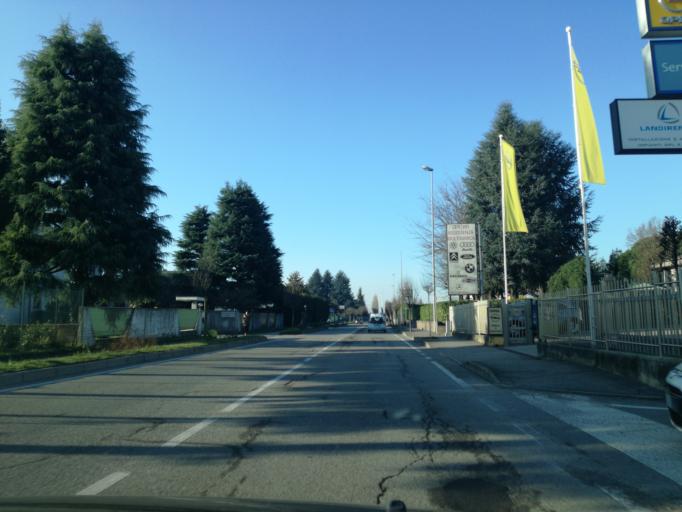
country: IT
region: Lombardy
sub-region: Provincia di Monza e Brianza
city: Bernareggio
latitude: 45.6423
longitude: 9.4017
